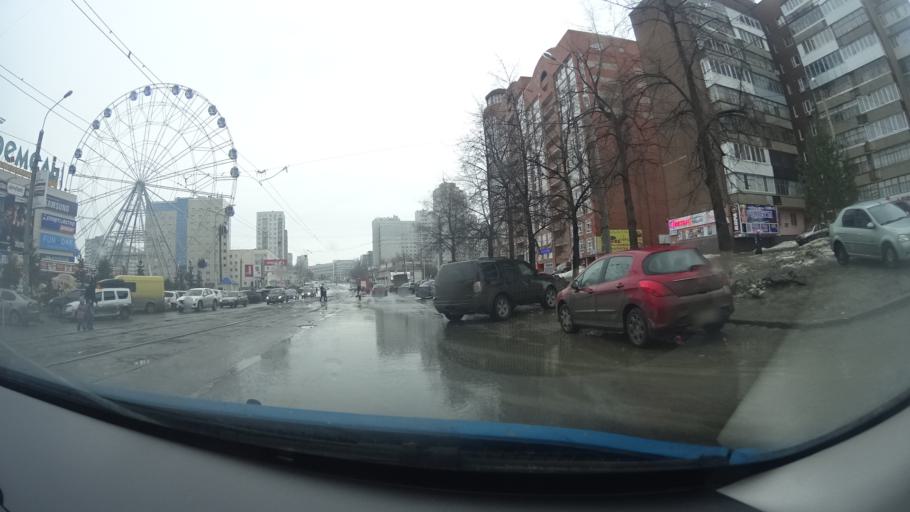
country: RU
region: Bashkortostan
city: Ufa
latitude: 54.7128
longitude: 55.9946
